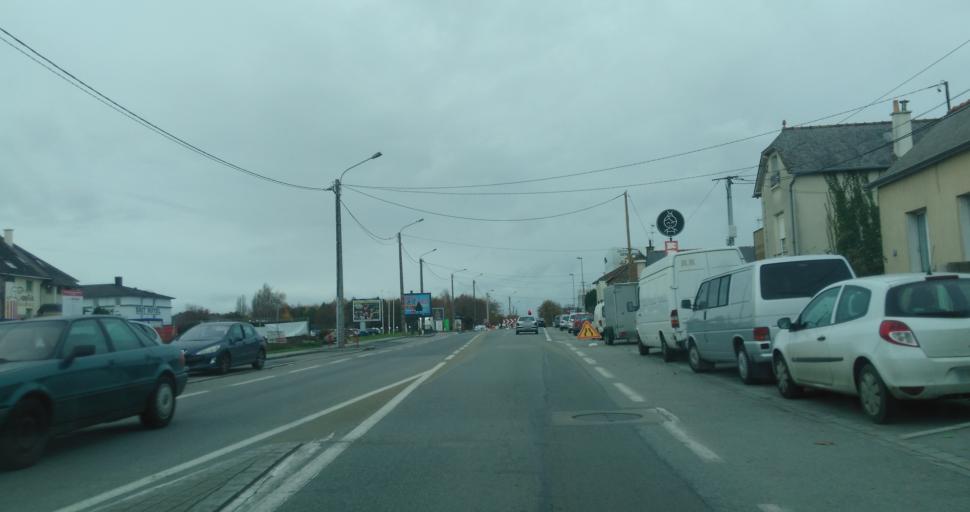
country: FR
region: Brittany
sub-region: Departement d'Ille-et-Vilaine
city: Chantepie
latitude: 48.0933
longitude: -1.6318
